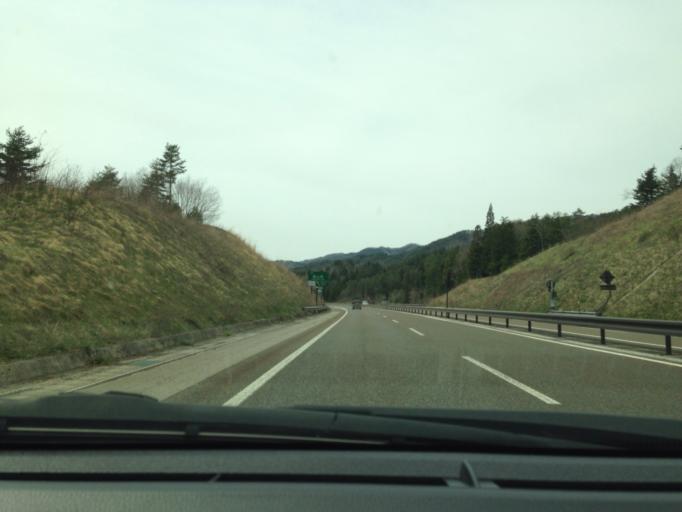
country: JP
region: Gifu
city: Takayama
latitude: 36.1385
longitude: 137.1761
